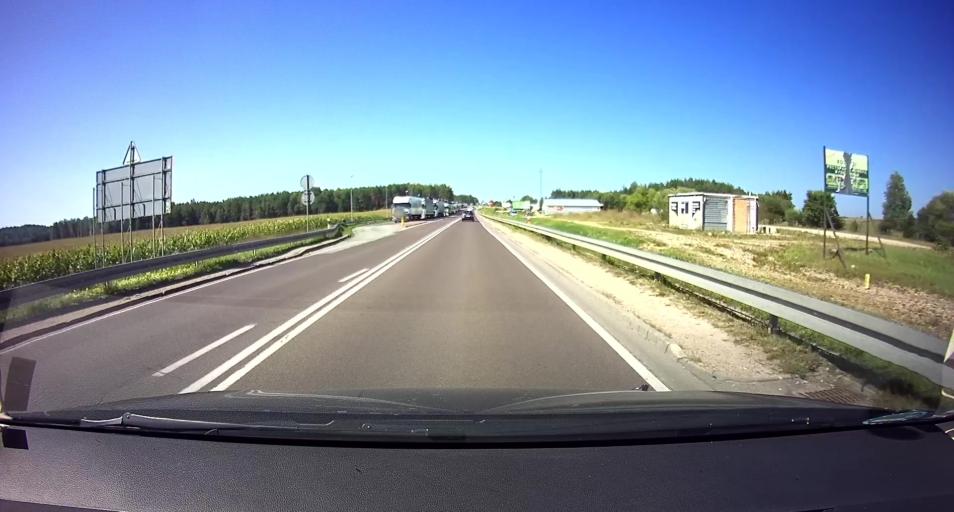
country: BY
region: Grodnenskaya
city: Vyalikaya Byerastavitsa
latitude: 53.1241
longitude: 23.8802
